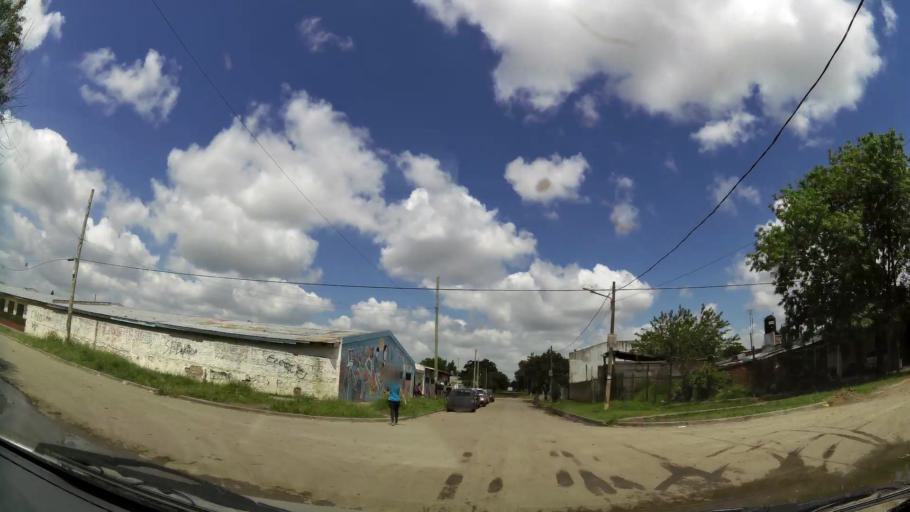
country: AR
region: Buenos Aires
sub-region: Partido de Quilmes
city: Quilmes
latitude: -34.8398
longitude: -58.2320
